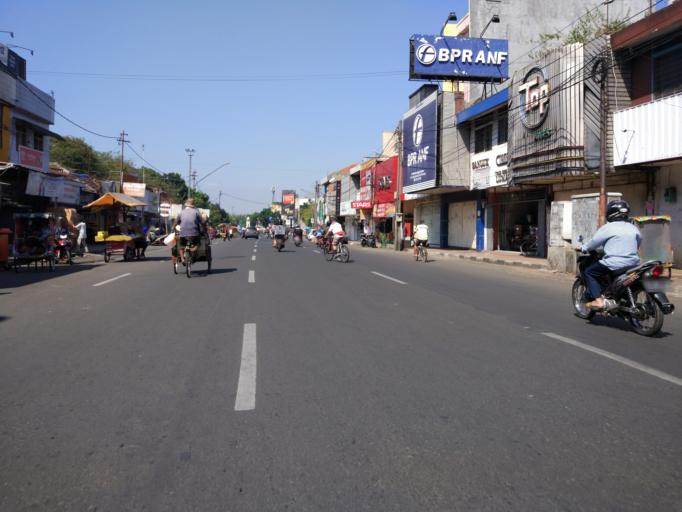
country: ID
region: West Java
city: Bandung
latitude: -6.9325
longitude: 107.6033
